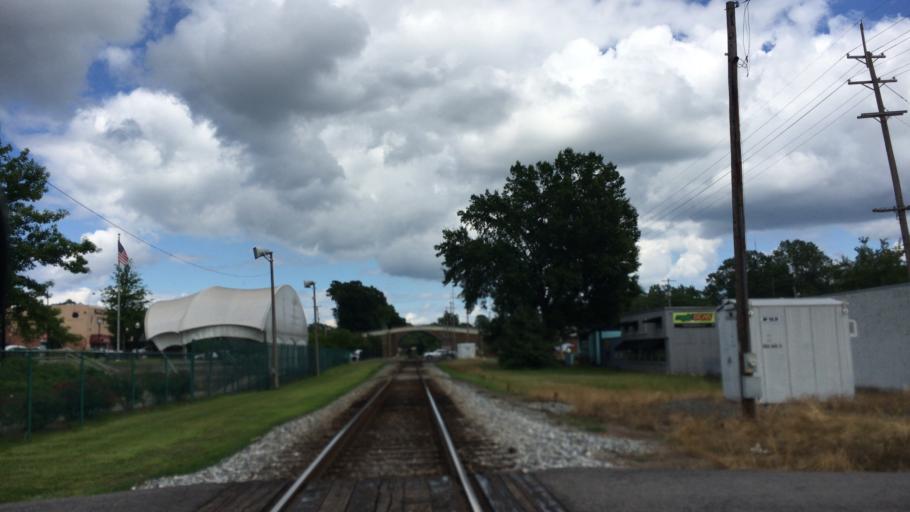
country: US
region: Louisiana
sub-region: Lincoln Parish
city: Ruston
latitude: 32.5287
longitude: -92.6393
